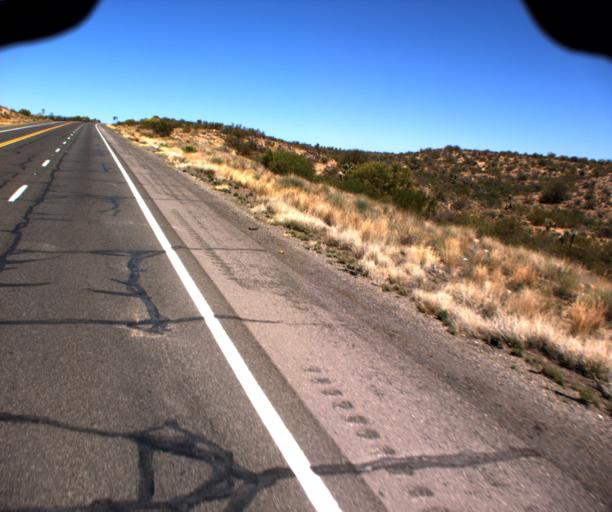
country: US
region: Arizona
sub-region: Yavapai County
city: Congress
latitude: 34.2190
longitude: -113.0681
